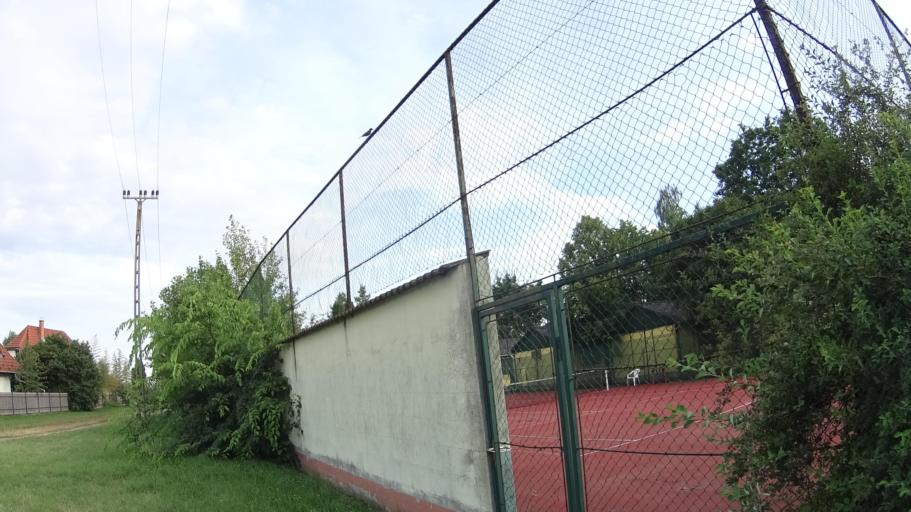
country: HU
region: Pest
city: Delegyhaza
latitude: 47.2608
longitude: 19.0955
